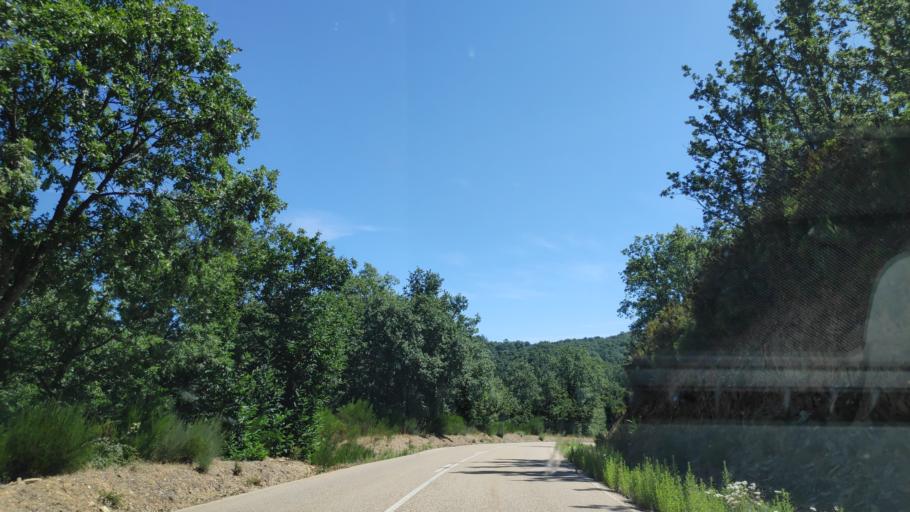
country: ES
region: Castille and Leon
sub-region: Provincia de Zamora
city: Requejo
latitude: 42.0228
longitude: -6.6953
